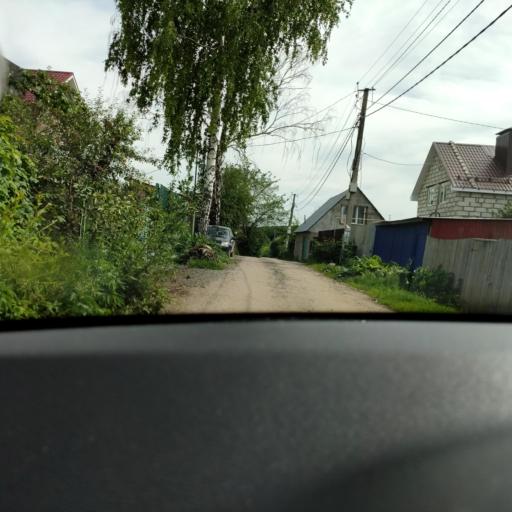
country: RU
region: Samara
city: Petra-Dubrava
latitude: 53.2830
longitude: 50.2872
